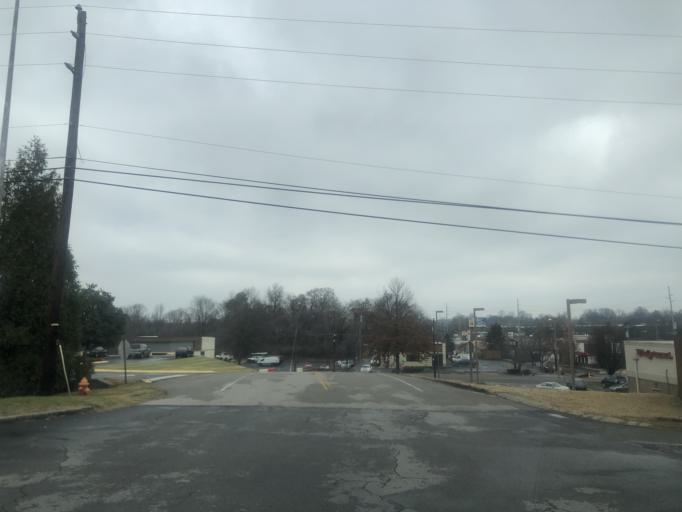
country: US
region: Tennessee
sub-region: Davidson County
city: Lakewood
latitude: 36.1479
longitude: -86.6677
